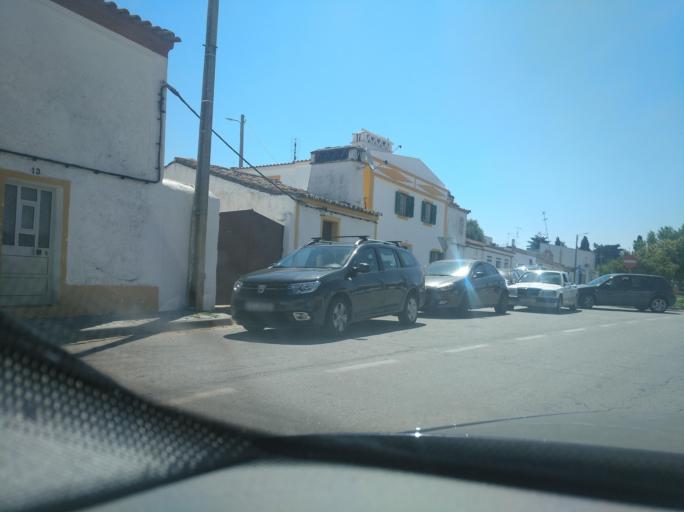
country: PT
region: Portalegre
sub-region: Elvas
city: Elvas
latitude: 38.9597
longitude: -7.2968
